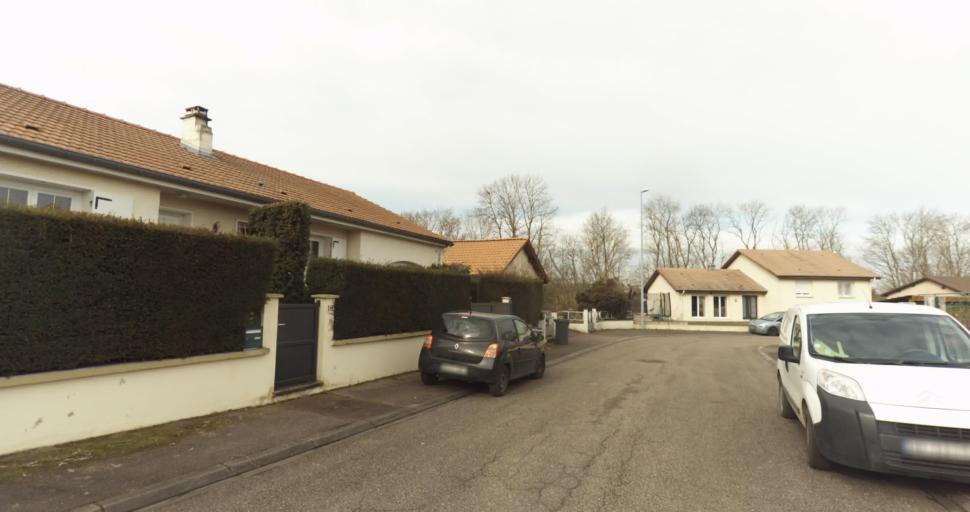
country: FR
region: Lorraine
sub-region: Departement de Meurthe-et-Moselle
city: Jarny
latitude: 49.1584
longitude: 5.8678
